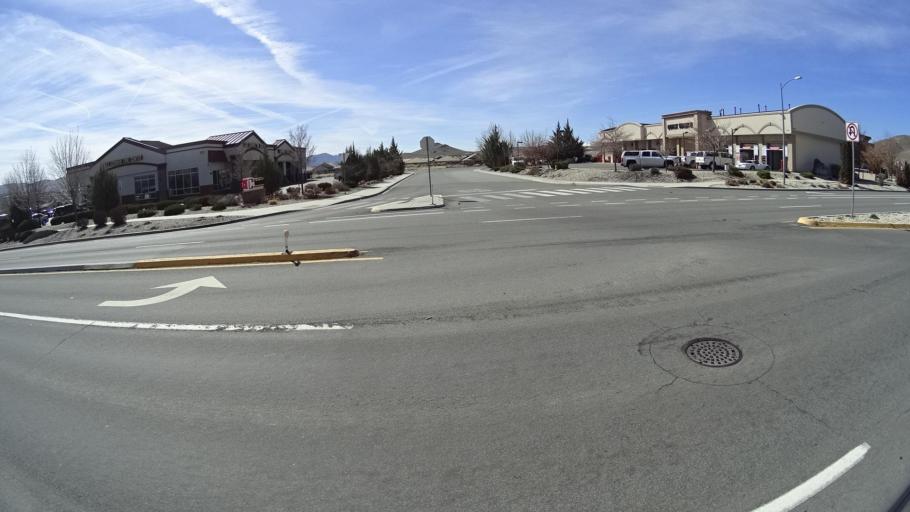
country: US
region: Nevada
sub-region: Washoe County
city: Sun Valley
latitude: 39.5854
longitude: -119.7361
